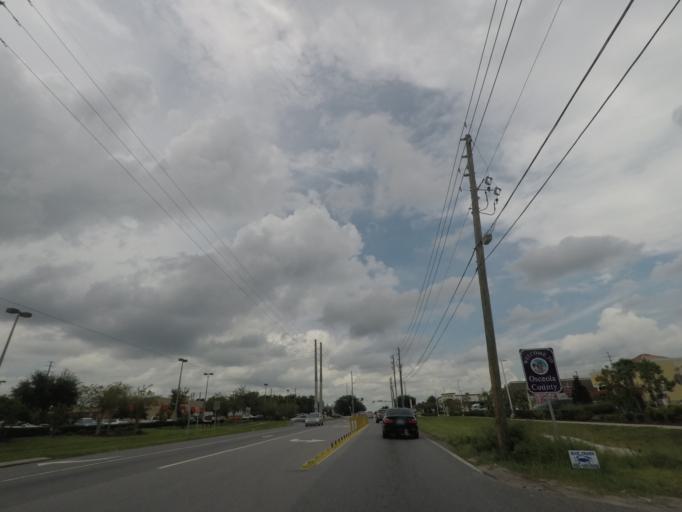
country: US
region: Florida
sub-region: Polk County
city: Loughman
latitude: 28.2582
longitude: -81.5906
